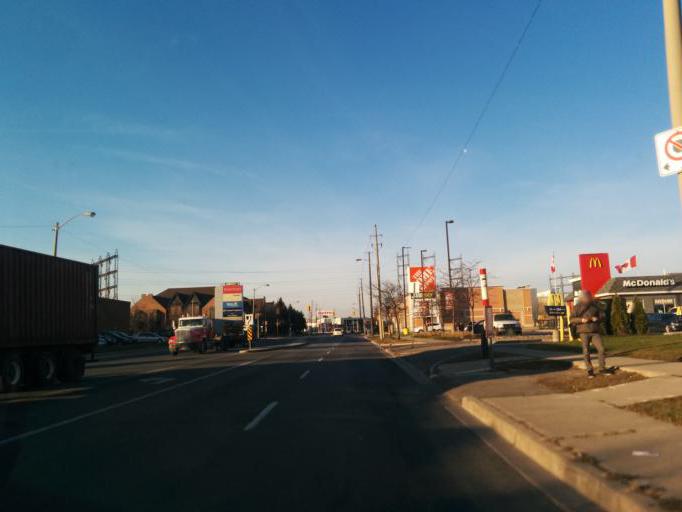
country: CA
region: Ontario
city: Etobicoke
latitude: 43.6150
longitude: -79.5563
